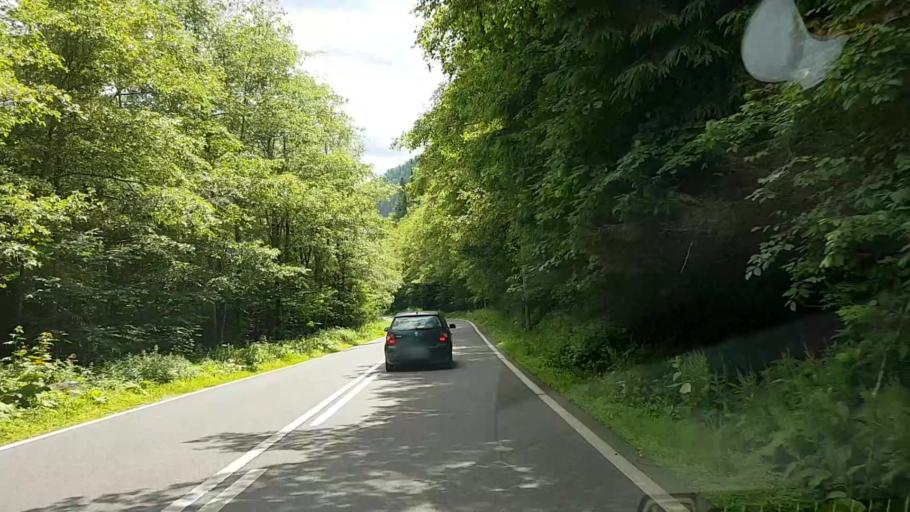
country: RO
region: Suceava
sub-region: Comuna Crucea
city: Crucea
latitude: 47.2905
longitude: 25.6329
